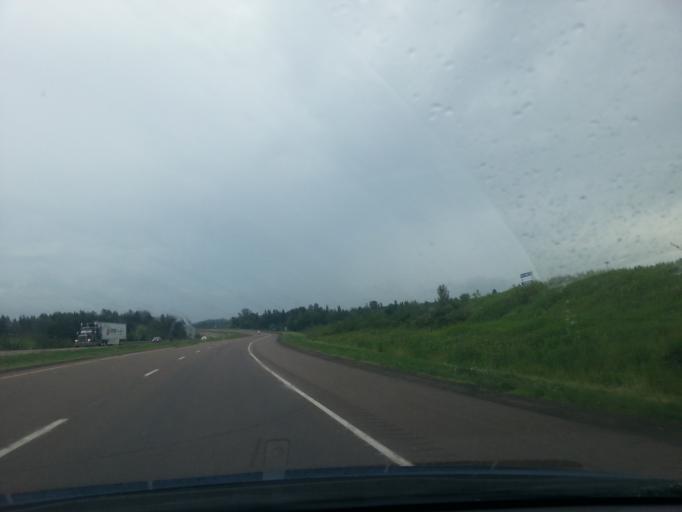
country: CA
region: New Brunswick
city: Moncton
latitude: 46.1318
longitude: -64.8726
